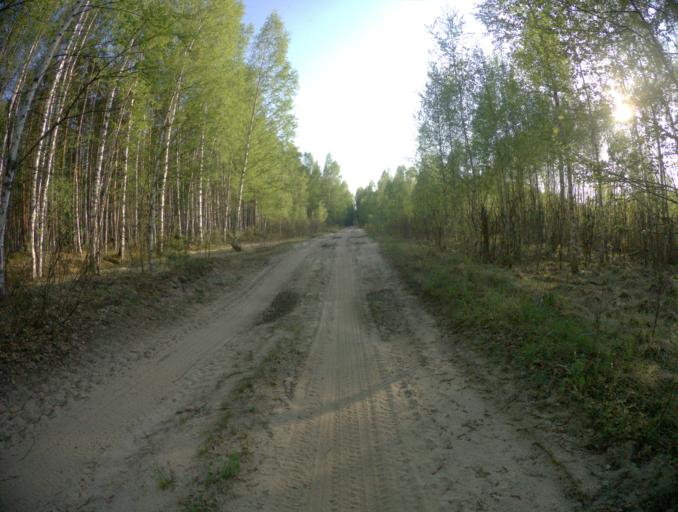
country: RU
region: Vladimir
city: Vyazniki
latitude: 56.3757
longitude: 42.1720
